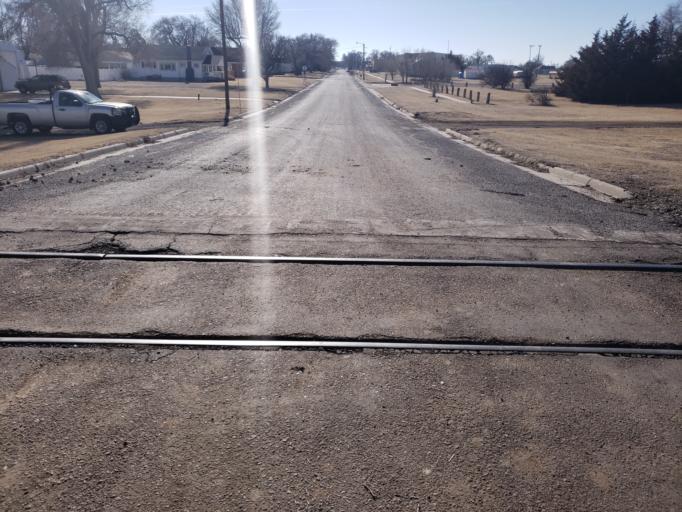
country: US
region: Kansas
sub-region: Ness County
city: Ness City
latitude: 38.4448
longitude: -99.6943
